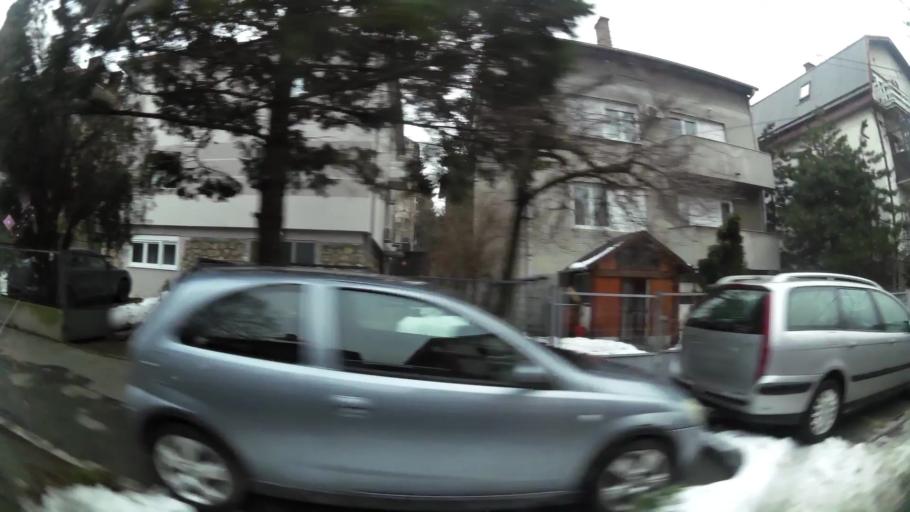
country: RS
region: Central Serbia
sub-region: Belgrade
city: Vozdovac
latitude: 44.7775
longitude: 20.4923
